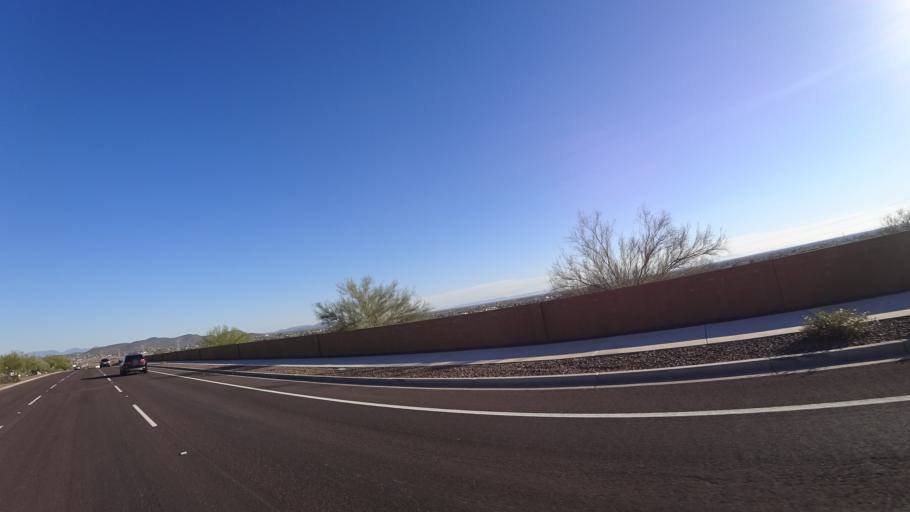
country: US
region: Arizona
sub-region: Maricopa County
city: Sun City West
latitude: 33.7102
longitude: -112.2438
